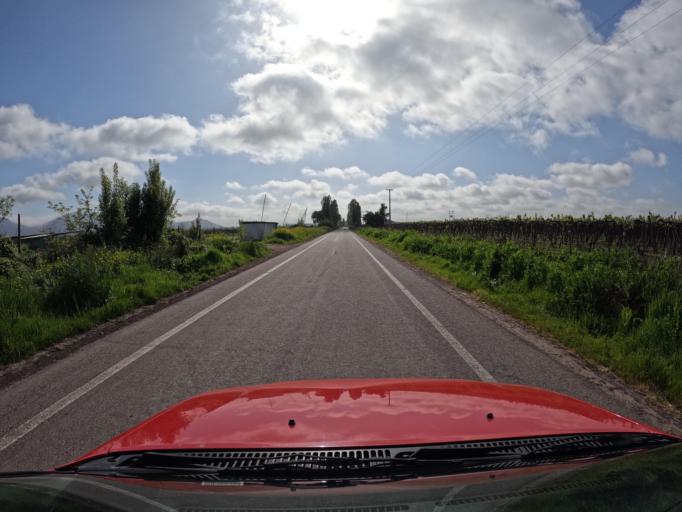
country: CL
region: Maule
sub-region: Provincia de Curico
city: Rauco
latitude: -34.8850
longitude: -71.2542
